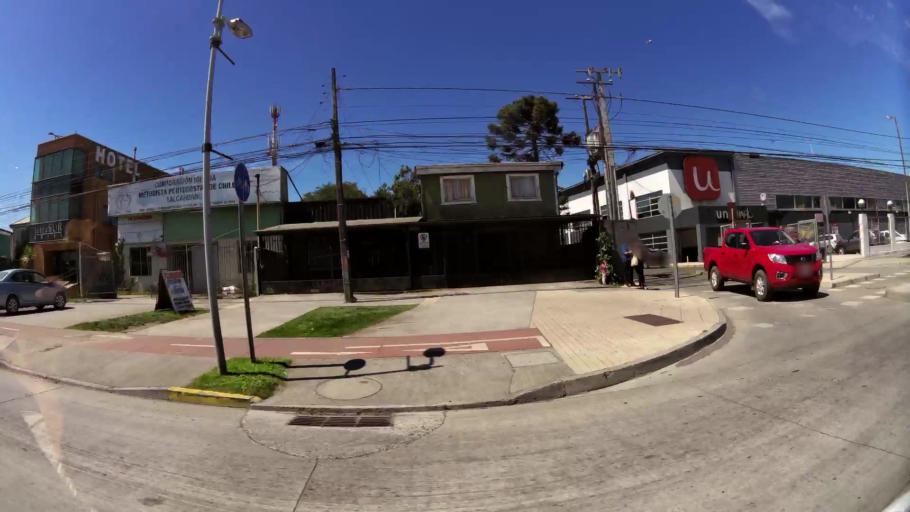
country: CL
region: Biobio
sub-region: Provincia de Concepcion
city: Talcahuano
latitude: -36.7516
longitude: -73.0927
